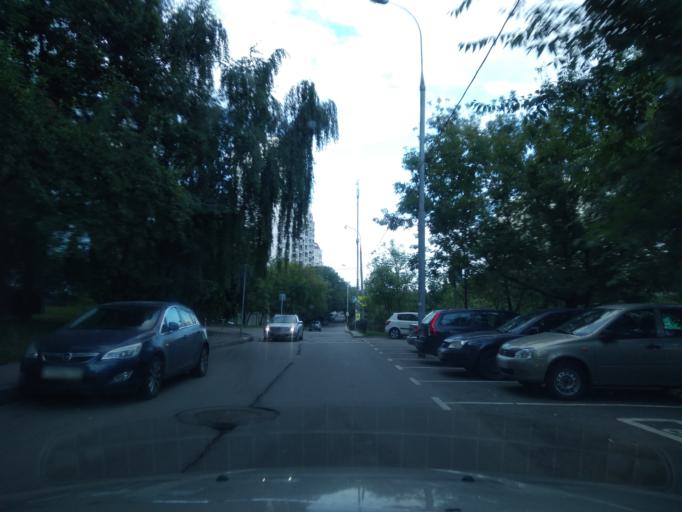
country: RU
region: Moscow
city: Strogino
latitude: 55.8144
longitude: 37.3997
